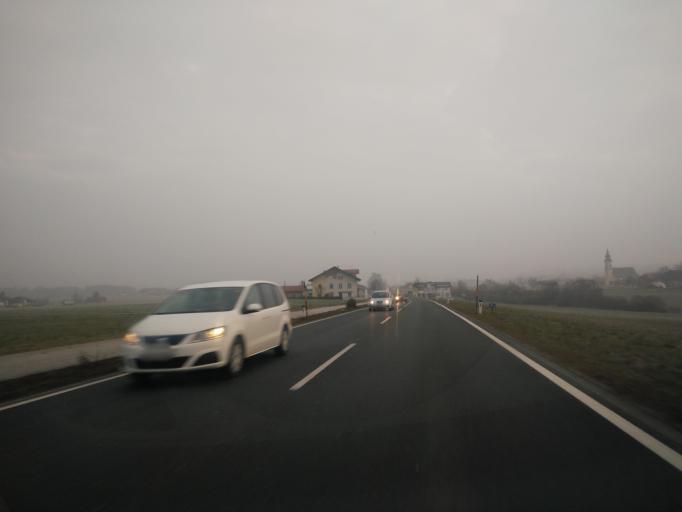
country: AT
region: Salzburg
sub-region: Politischer Bezirk Salzburg-Umgebung
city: Lamprechtshausen
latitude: 47.9645
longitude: 12.9479
